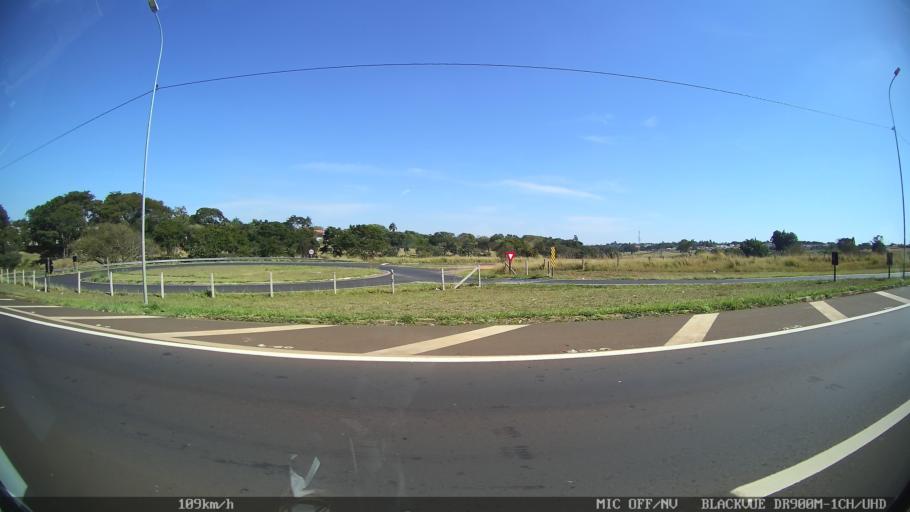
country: BR
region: Sao Paulo
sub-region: Franca
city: Franca
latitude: -20.4845
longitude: -47.4097
